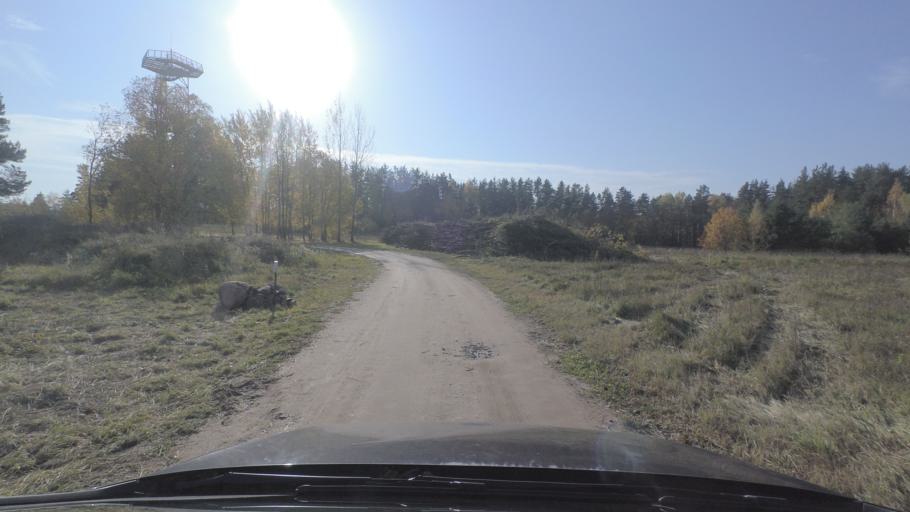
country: LT
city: Ignalina
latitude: 55.3353
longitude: 26.1771
